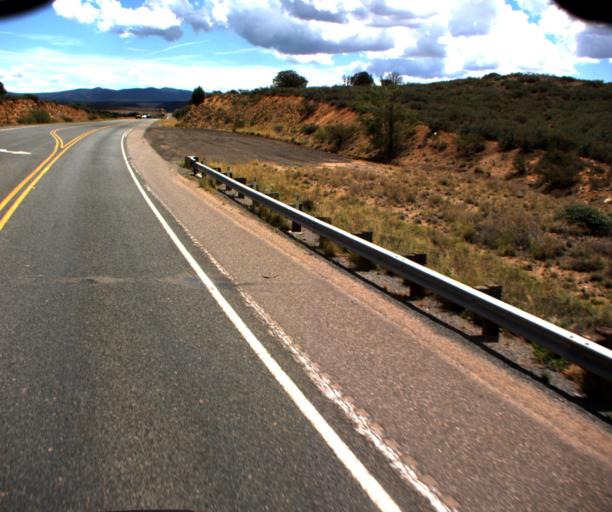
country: US
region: Arizona
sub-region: Yavapai County
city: Verde Village
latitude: 34.5235
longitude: -112.0460
